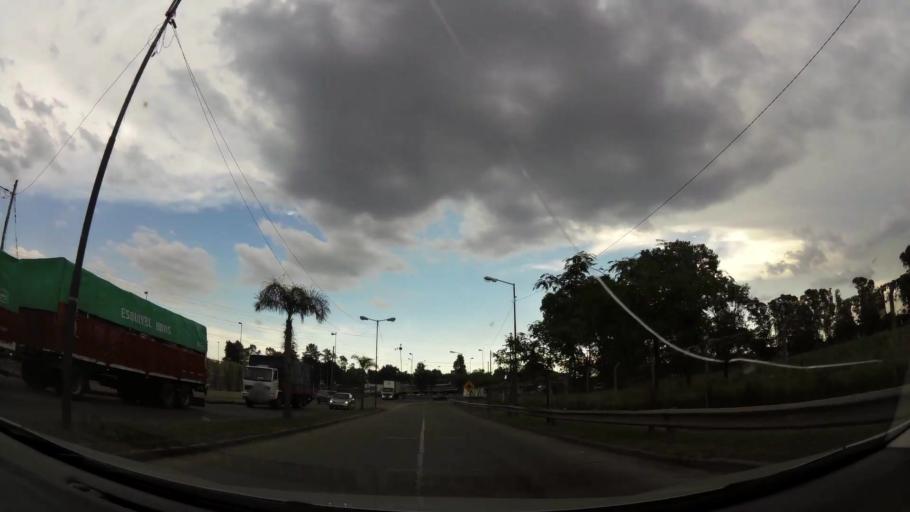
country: AR
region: Buenos Aires
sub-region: Partido de Tigre
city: Tigre
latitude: -34.4859
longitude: -58.5930
